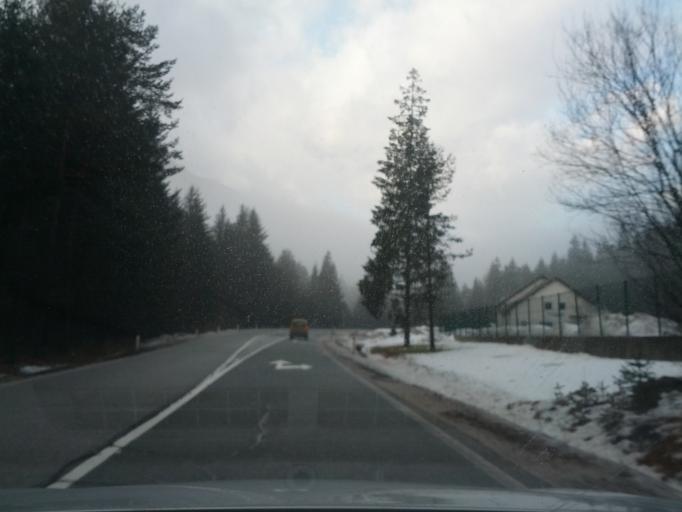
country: SI
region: Kranjska Gora
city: Mojstrana
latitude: 46.4785
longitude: 13.8770
